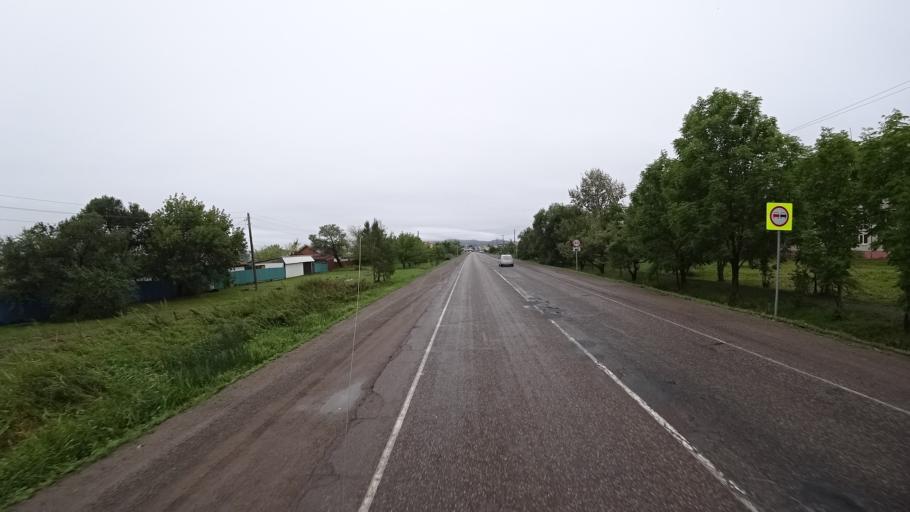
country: RU
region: Primorskiy
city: Monastyrishche
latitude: 44.2074
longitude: 132.4500
